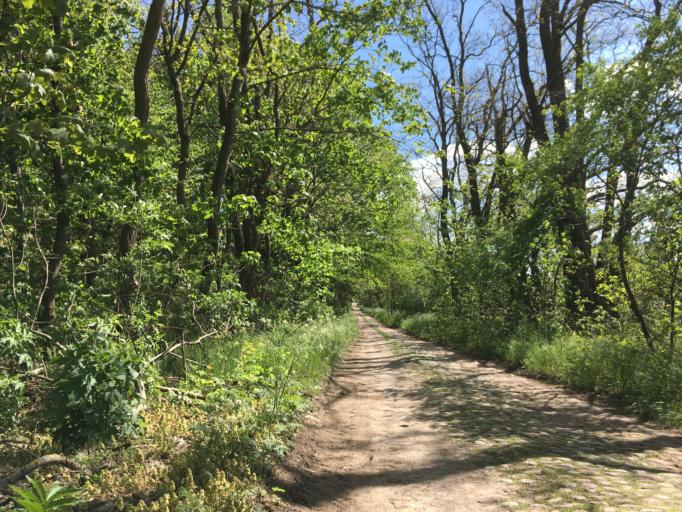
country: DE
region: Brandenburg
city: Rudnitz
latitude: 52.6719
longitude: 13.6735
